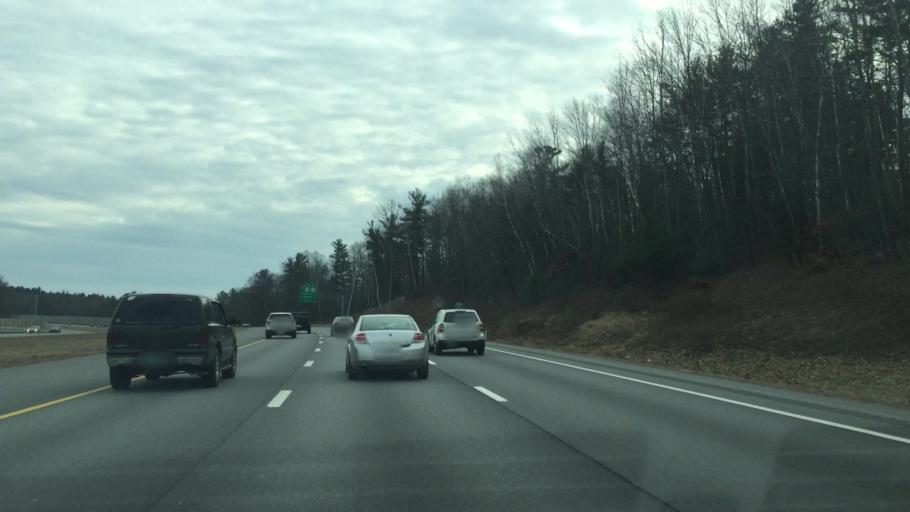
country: US
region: New Hampshire
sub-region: Rockingham County
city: Windham
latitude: 42.7889
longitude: -71.2694
